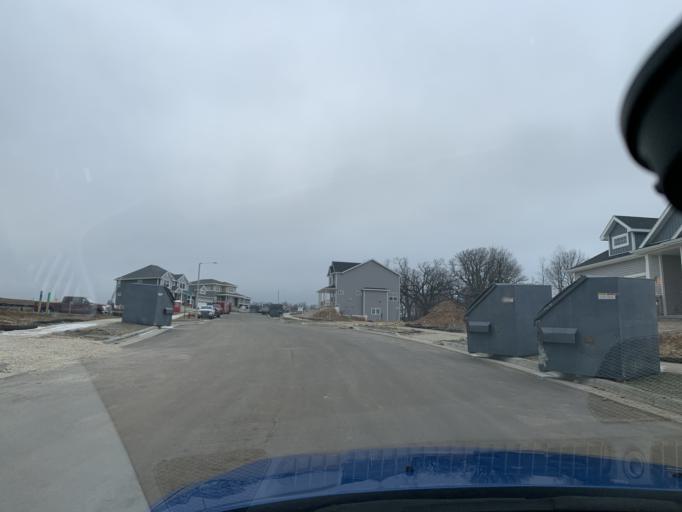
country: US
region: Wisconsin
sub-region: Dane County
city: Middleton
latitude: 43.0687
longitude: -89.5658
